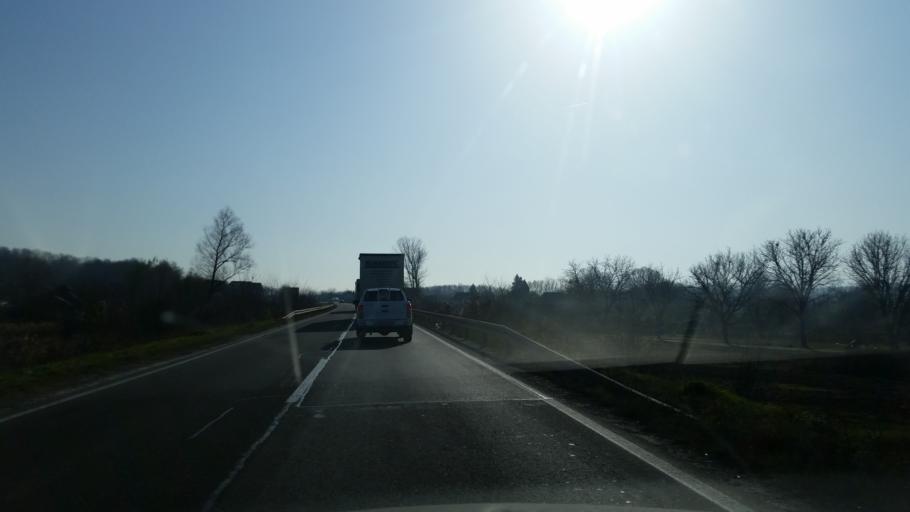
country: RS
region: Central Serbia
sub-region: Belgrade
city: Lazarevac
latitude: 44.3250
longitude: 20.2229
